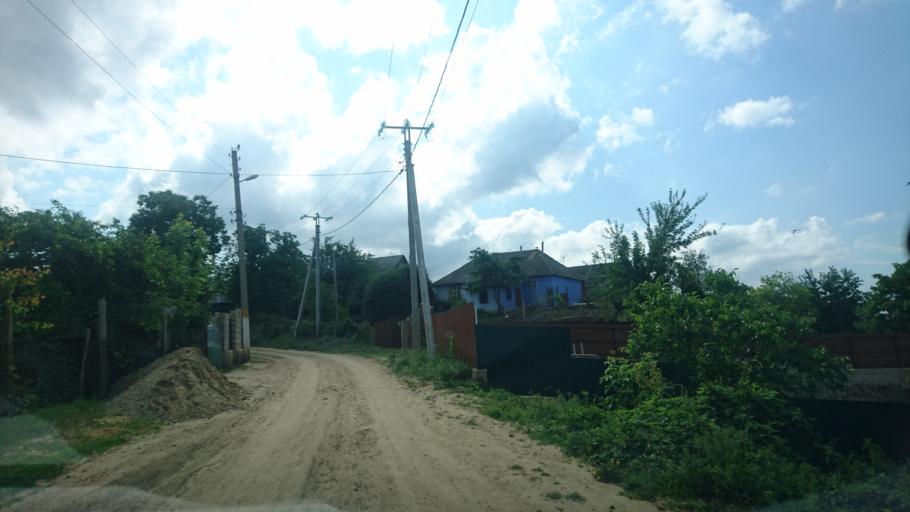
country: MD
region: Telenesti
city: Cocieri
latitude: 47.3613
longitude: 29.1015
